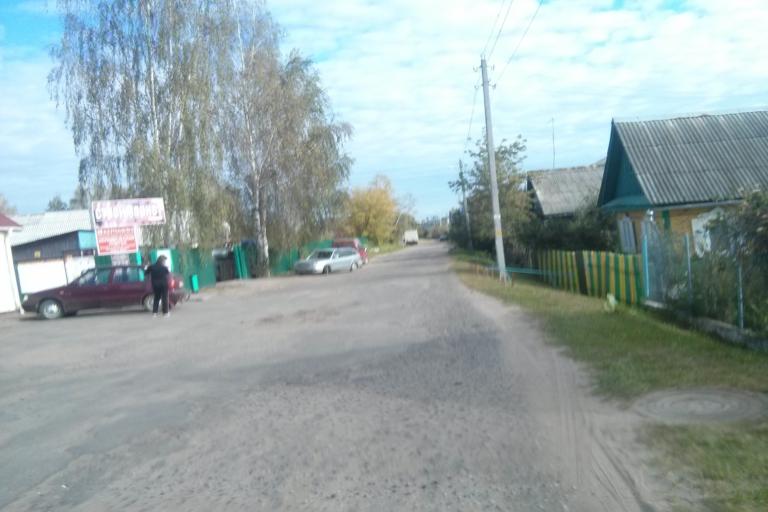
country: BY
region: Minsk
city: Chervyen'
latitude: 53.7151
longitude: 28.4209
